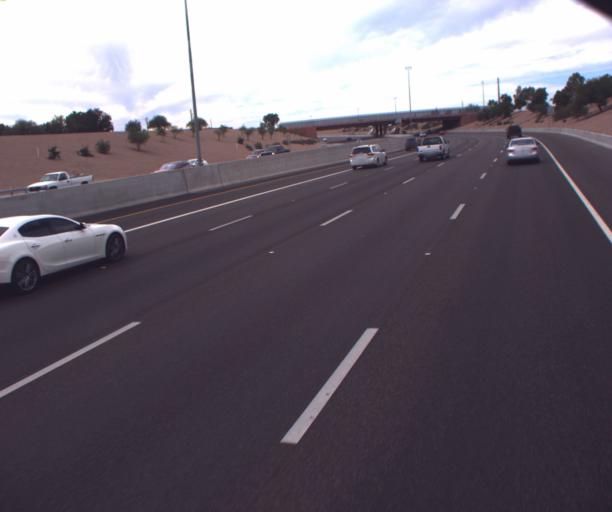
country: US
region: Arizona
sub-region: Maricopa County
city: Mesa
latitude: 33.4661
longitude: -111.8192
